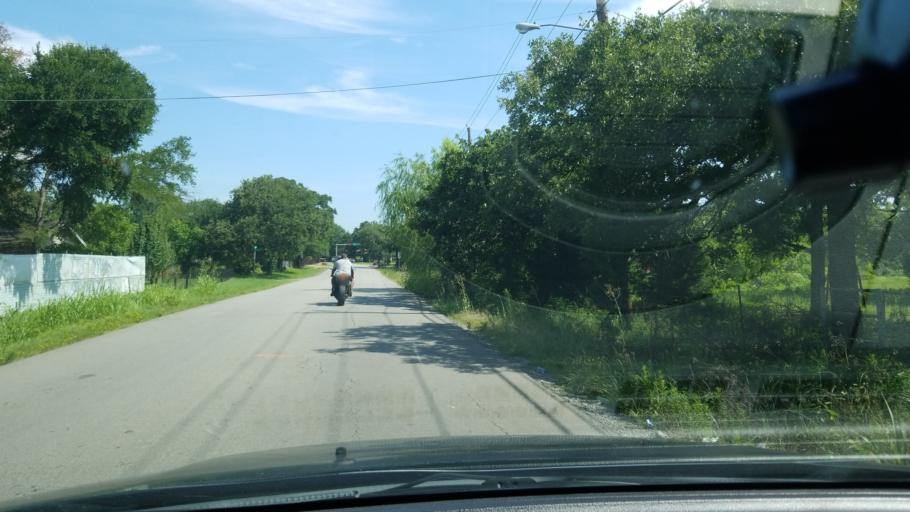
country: US
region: Texas
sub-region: Dallas County
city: Balch Springs
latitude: 32.7322
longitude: -96.6392
